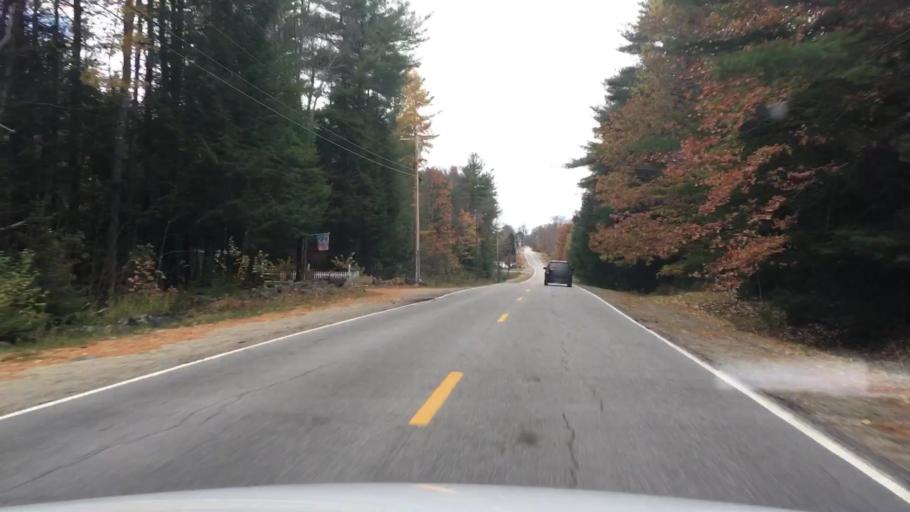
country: US
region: Maine
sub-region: Kennebec County
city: Monmouth
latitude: 44.1901
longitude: -70.0687
